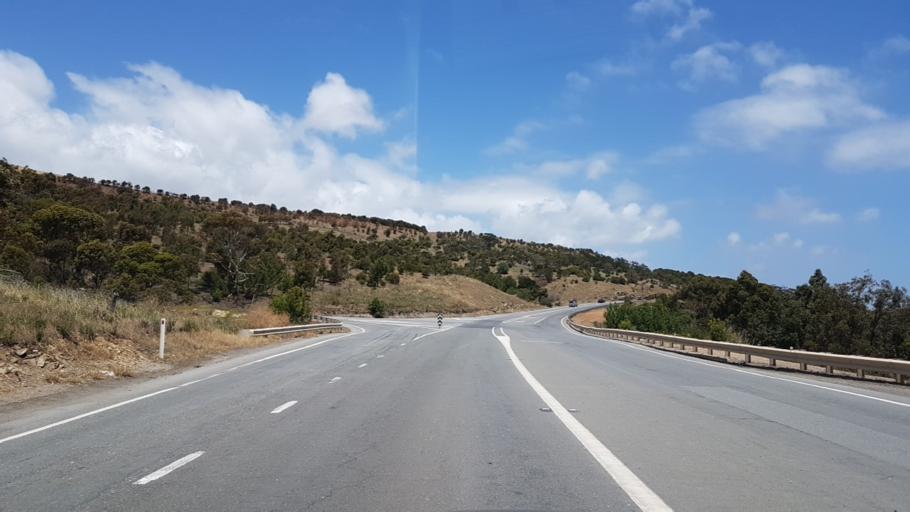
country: AU
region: South Australia
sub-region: Onkaparinga
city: Aldinga
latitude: -35.3336
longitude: 138.4700
